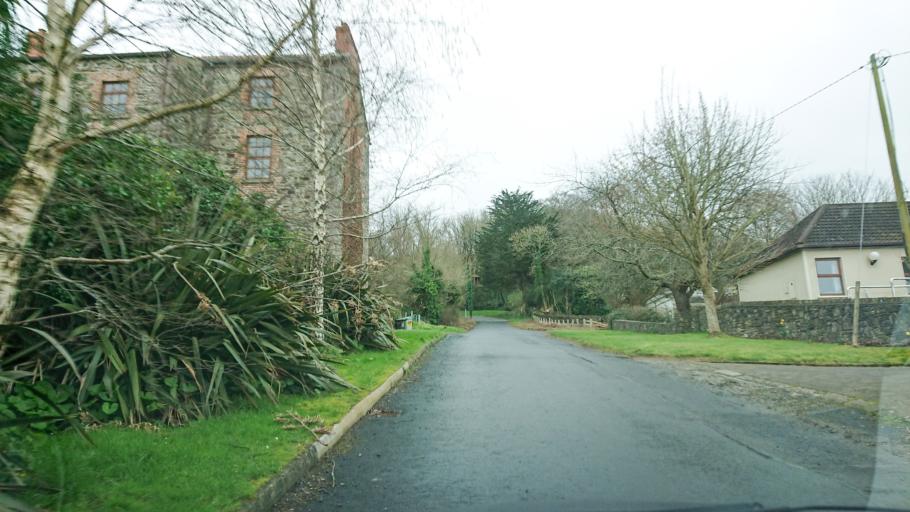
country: IE
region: Munster
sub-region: Waterford
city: Waterford
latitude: 52.2709
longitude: -7.0018
